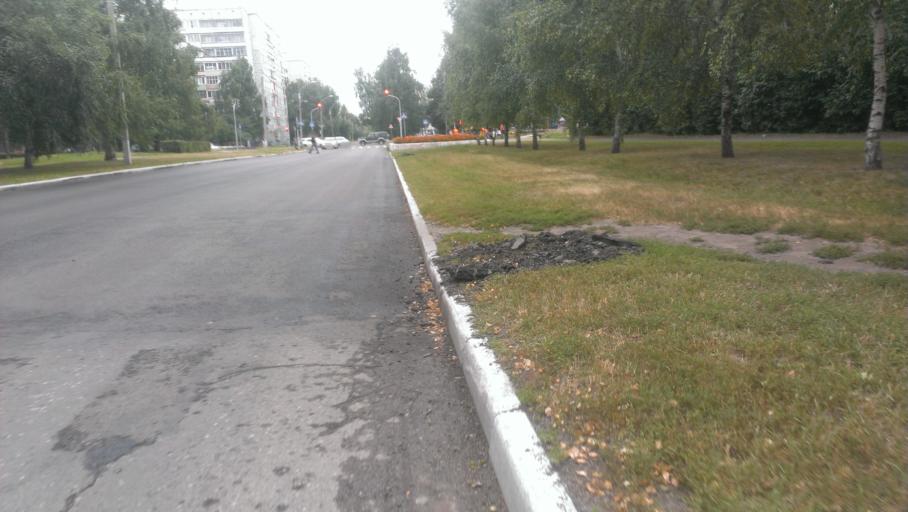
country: RU
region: Altai Krai
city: Novosilikatnyy
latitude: 53.3683
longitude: 83.6688
